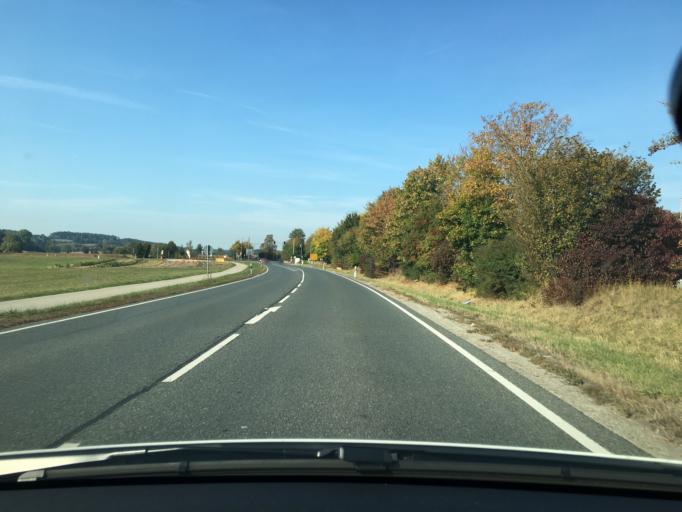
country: DE
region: Bavaria
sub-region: Regierungsbezirk Mittelfranken
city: Sachsen
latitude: 49.2847
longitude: 10.6625
